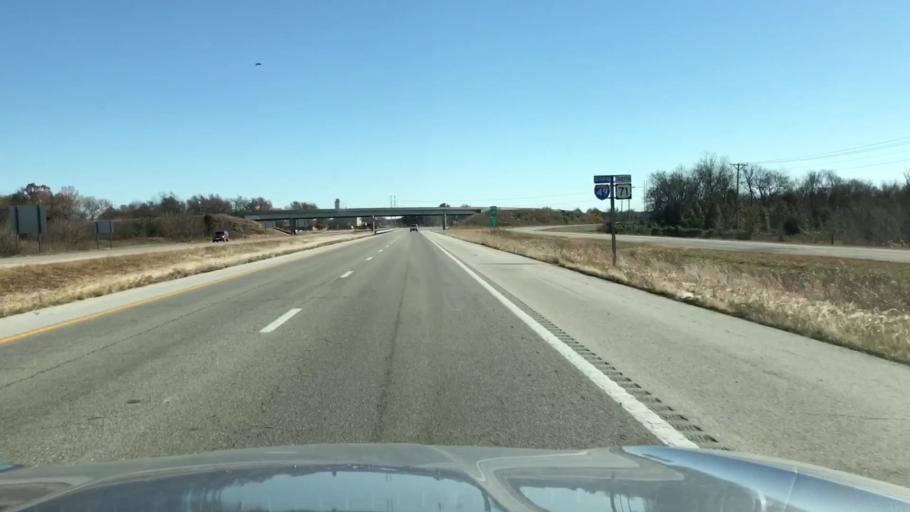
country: US
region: Missouri
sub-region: Jasper County
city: Carthage
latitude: 37.1349
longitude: -94.3163
